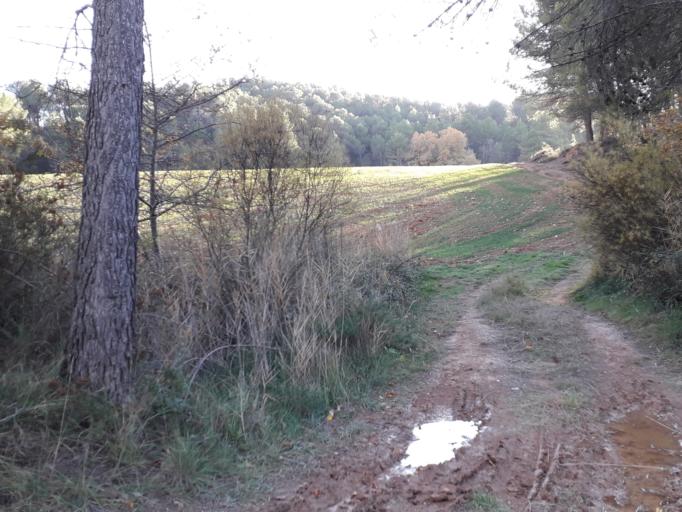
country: ES
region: Catalonia
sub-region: Provincia de Barcelona
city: Sant Marti de Tous
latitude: 41.5120
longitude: 1.5148
